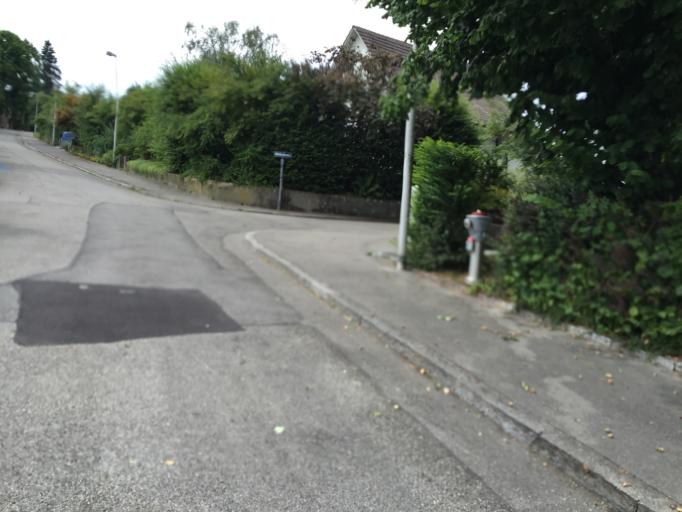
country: CH
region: Bern
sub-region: Bern-Mittelland District
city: Koniz
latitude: 46.9284
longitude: 7.4321
